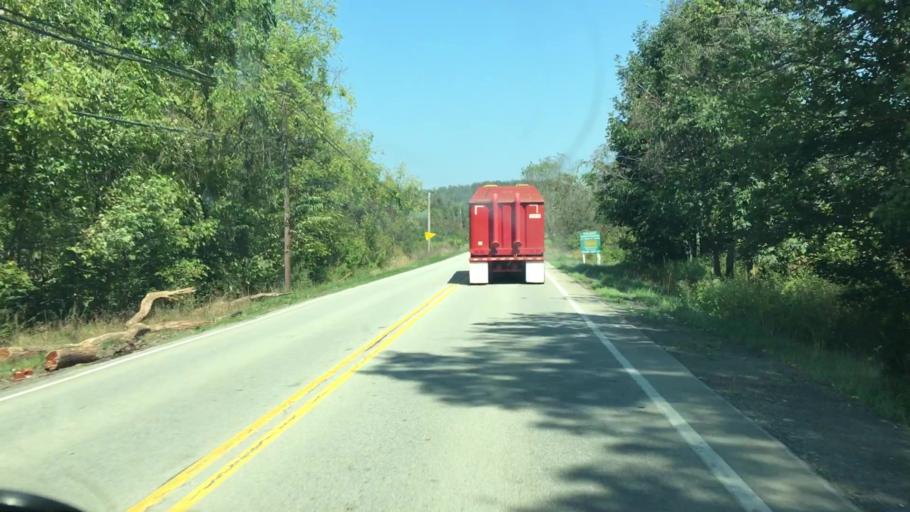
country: US
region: Pennsylvania
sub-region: Washington County
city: Washington
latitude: 40.1286
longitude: -80.2865
